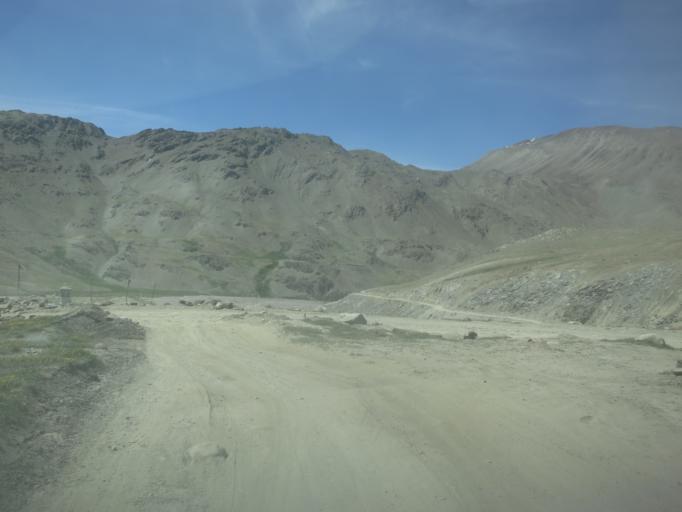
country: IN
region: Himachal Pradesh
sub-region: Kulu
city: Manali
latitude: 32.4054
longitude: 77.6439
